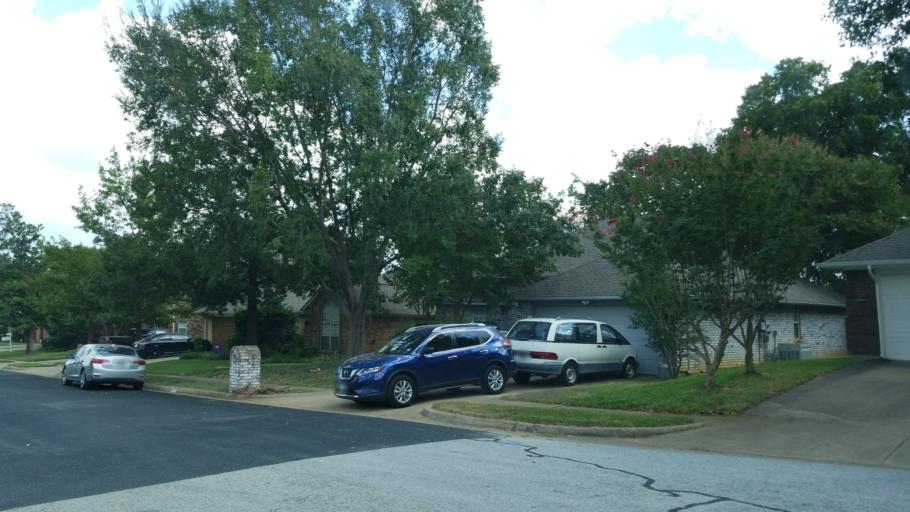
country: US
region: Texas
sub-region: Tarrant County
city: Euless
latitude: 32.8778
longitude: -97.0779
